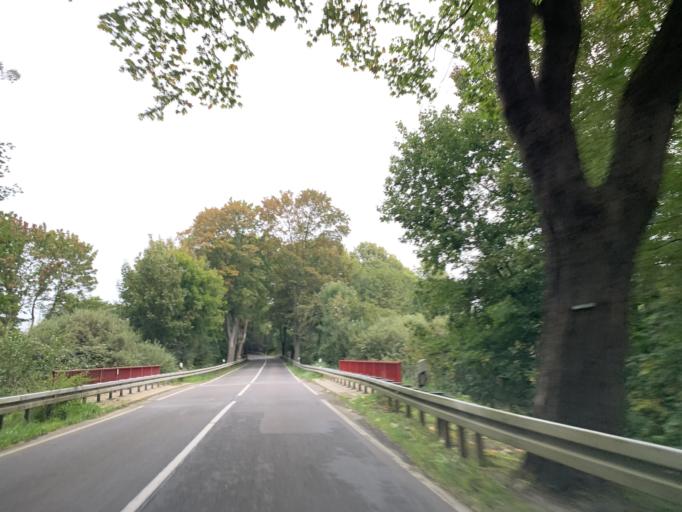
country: DE
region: Mecklenburg-Vorpommern
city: Loitz
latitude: 53.3329
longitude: 13.4907
